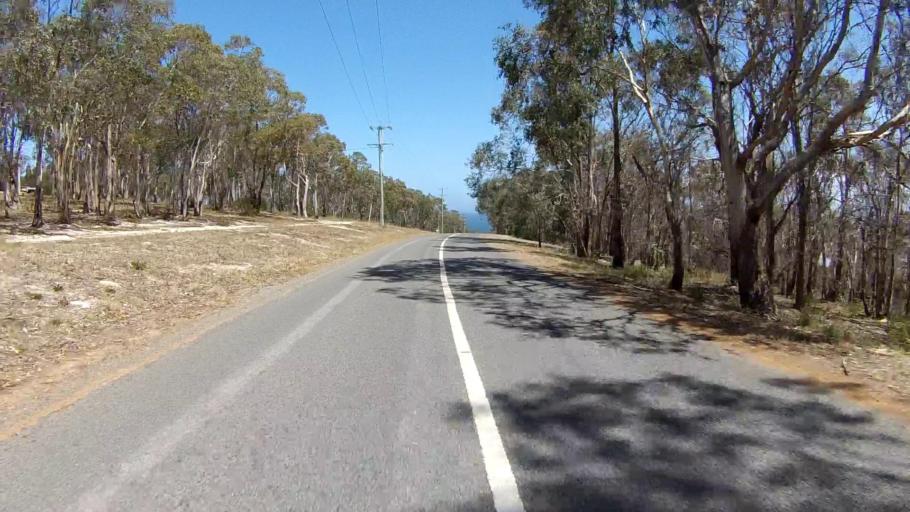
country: AU
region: Tasmania
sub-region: Clarence
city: Sandford
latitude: -43.0191
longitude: 147.4816
